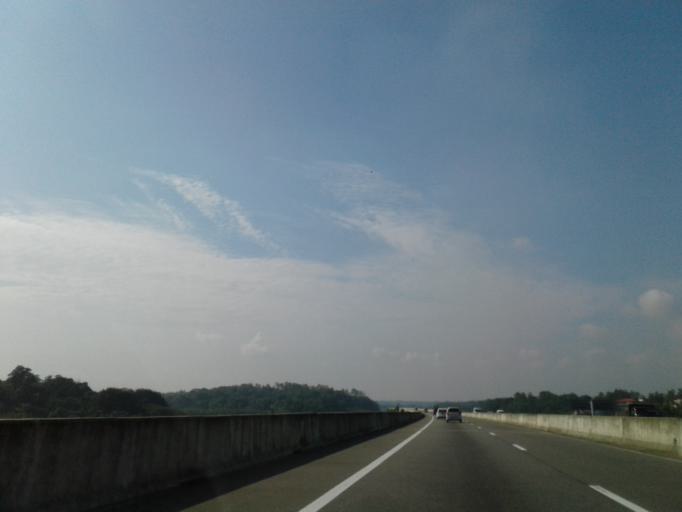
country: LK
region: Western
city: Mulleriyawa
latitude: 6.9067
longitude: 79.9804
